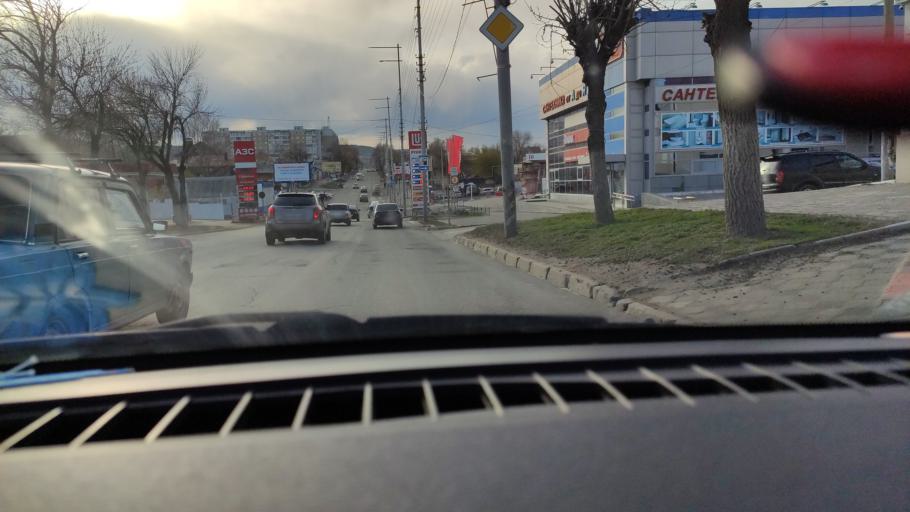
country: RU
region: Saratov
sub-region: Saratovskiy Rayon
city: Saratov
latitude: 51.5446
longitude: 46.0313
